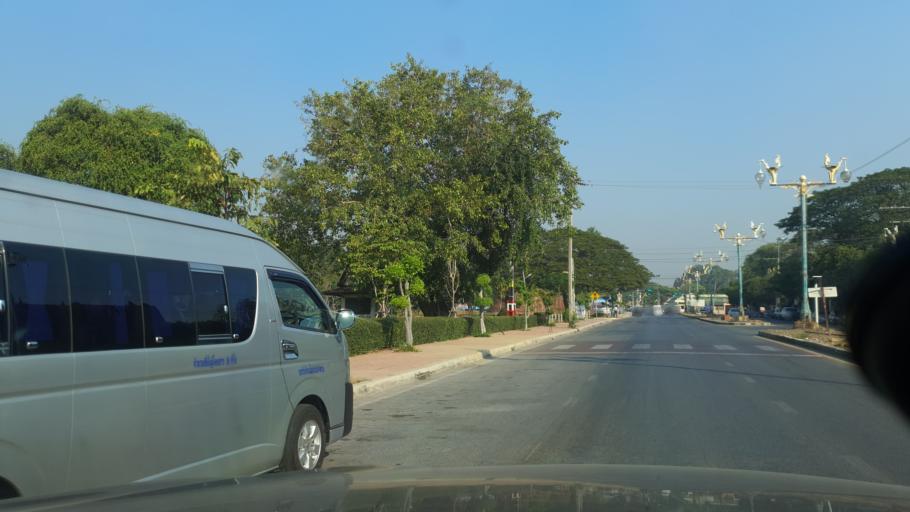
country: TH
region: Phra Nakhon Si Ayutthaya
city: Phra Nakhon Si Ayutthaya
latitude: 14.3591
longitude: 100.5685
